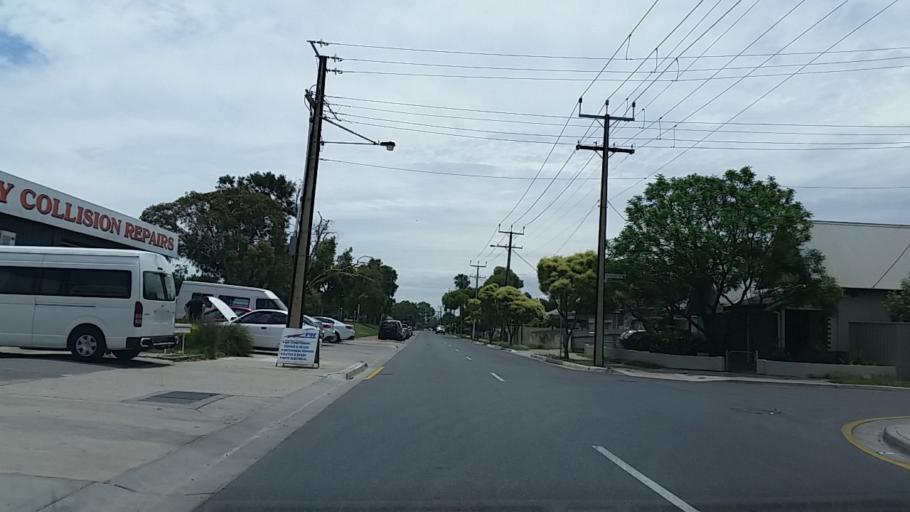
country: AU
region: South Australia
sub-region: Charles Sturt
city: Allenby Gardens
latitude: -34.9014
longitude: 138.5475
